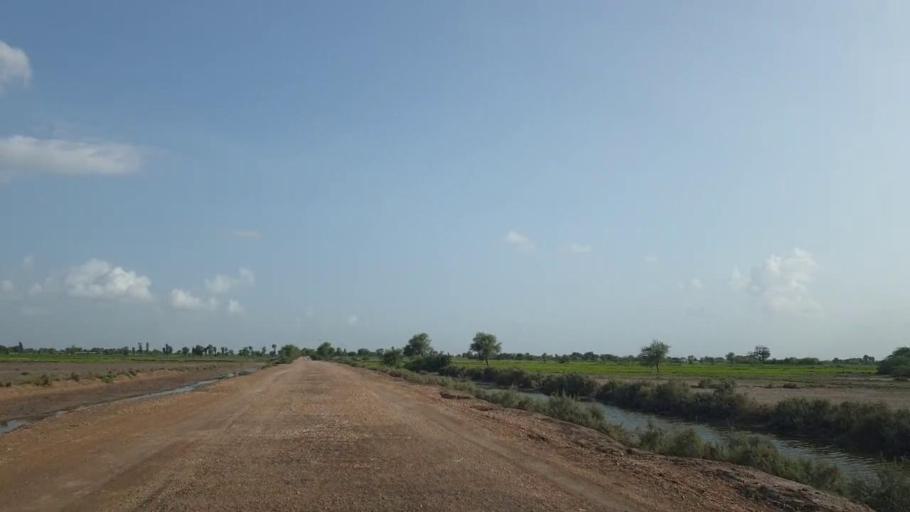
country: PK
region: Sindh
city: Kadhan
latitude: 24.6331
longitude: 69.0960
